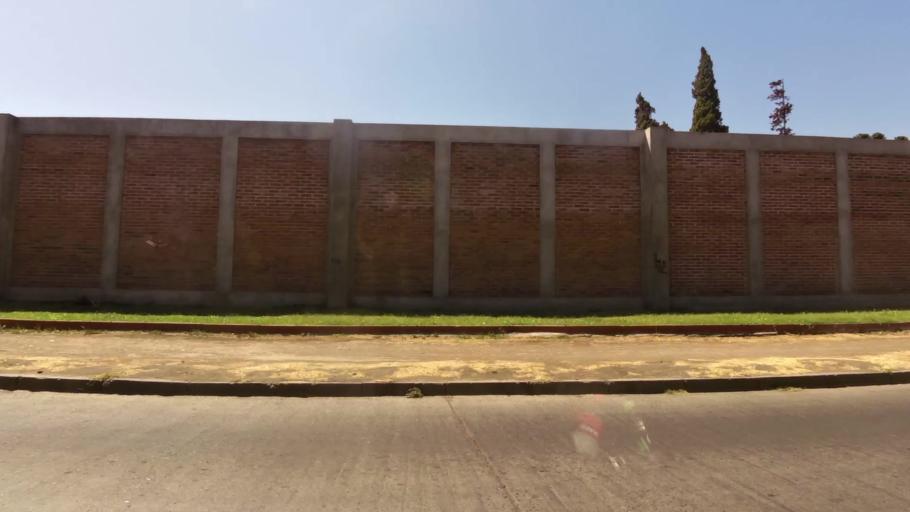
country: CL
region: Maule
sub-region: Provincia de Curico
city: Curico
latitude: -34.9764
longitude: -71.2355
